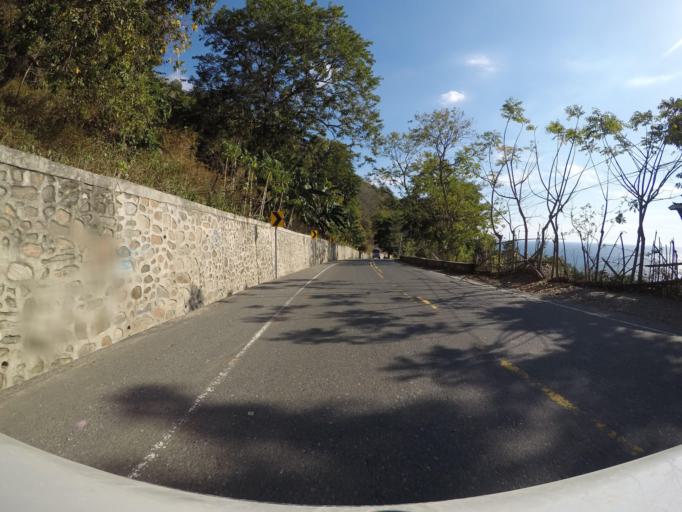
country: TL
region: Liquica
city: Maubara
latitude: -8.6636
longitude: 125.1139
